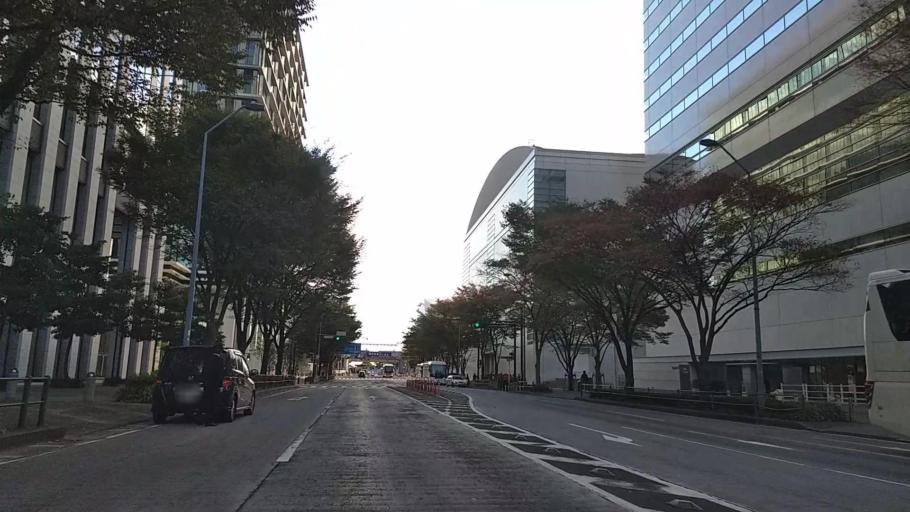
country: JP
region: Kanagawa
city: Yokohama
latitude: 35.4573
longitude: 139.6335
